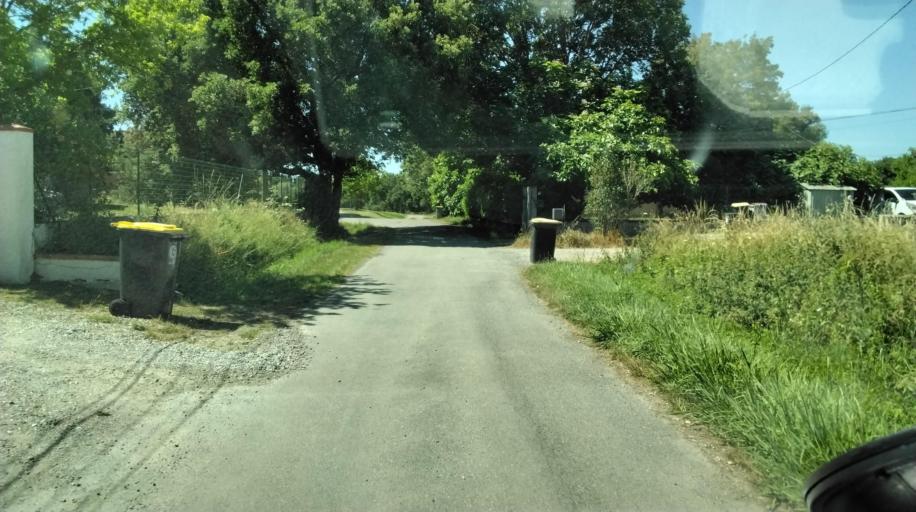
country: FR
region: Midi-Pyrenees
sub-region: Departement de la Haute-Garonne
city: Sainte-Foy-de-Peyrolieres
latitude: 43.4800
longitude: 1.1273
